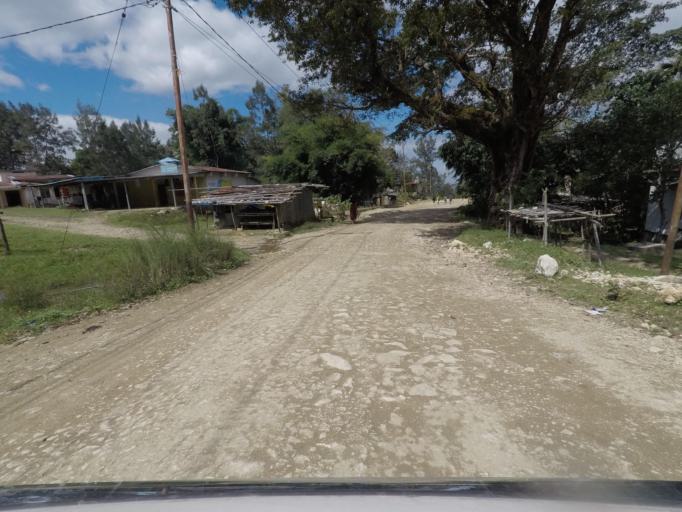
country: TL
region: Baucau
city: Venilale
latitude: -8.7364
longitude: 126.3717
